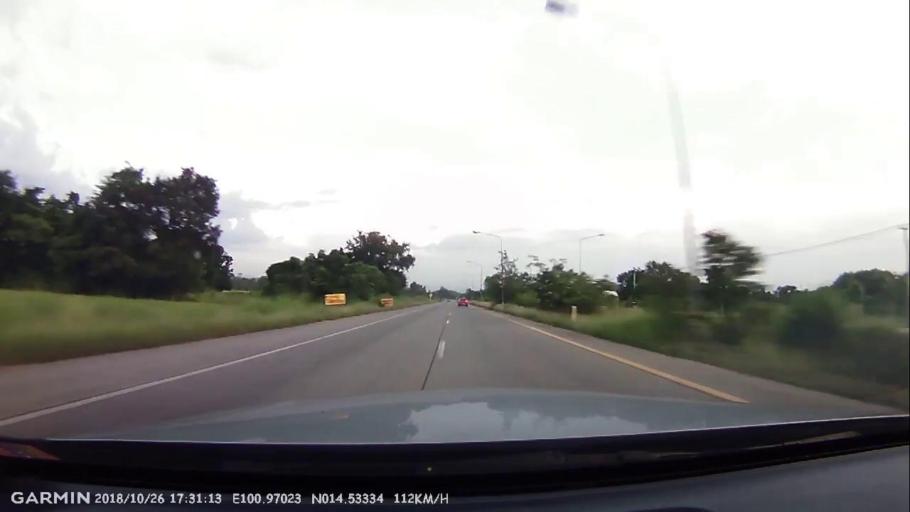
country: TH
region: Sara Buri
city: Saraburi
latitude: 14.5332
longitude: 100.9705
